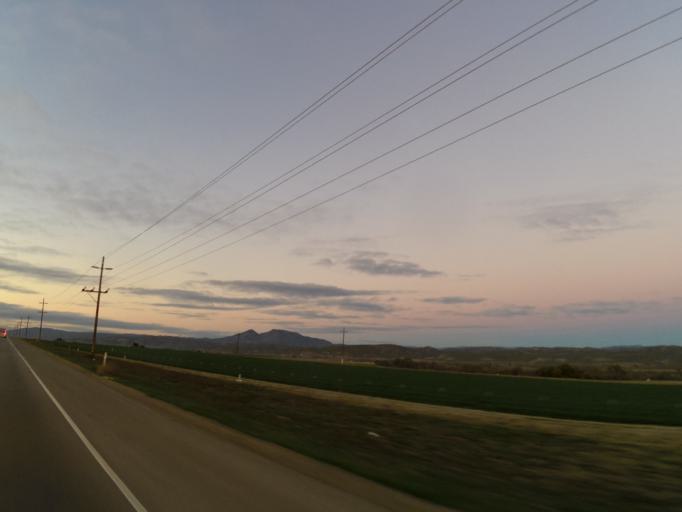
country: US
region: California
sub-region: Monterey County
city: Greenfield
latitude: 36.2762
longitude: -121.1854
